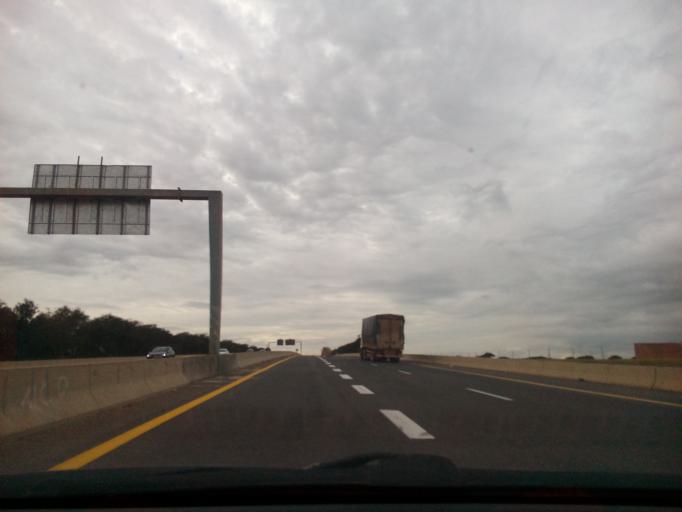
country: DZ
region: Mascara
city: Sig
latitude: 35.5420
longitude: -0.3460
